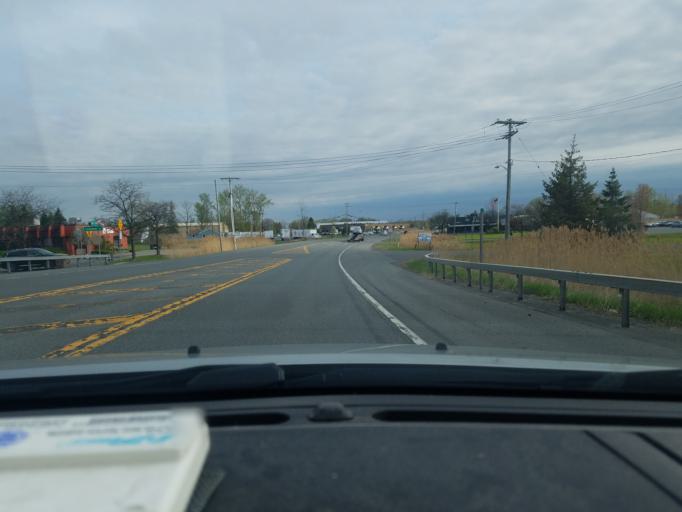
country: US
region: New York
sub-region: Onondaga County
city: East Syracuse
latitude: 43.0961
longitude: -76.0789
